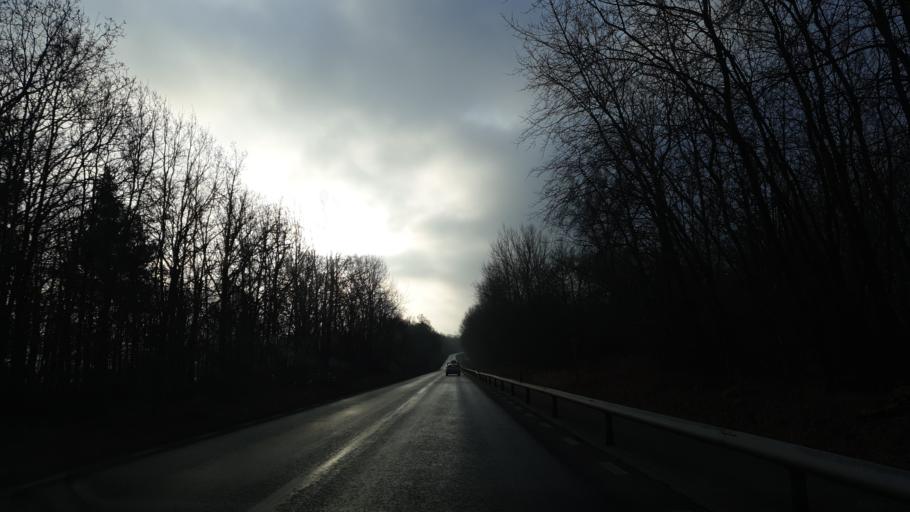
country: SE
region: Blekinge
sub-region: Karlshamns Kommun
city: Morrum
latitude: 56.1381
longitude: 14.6711
